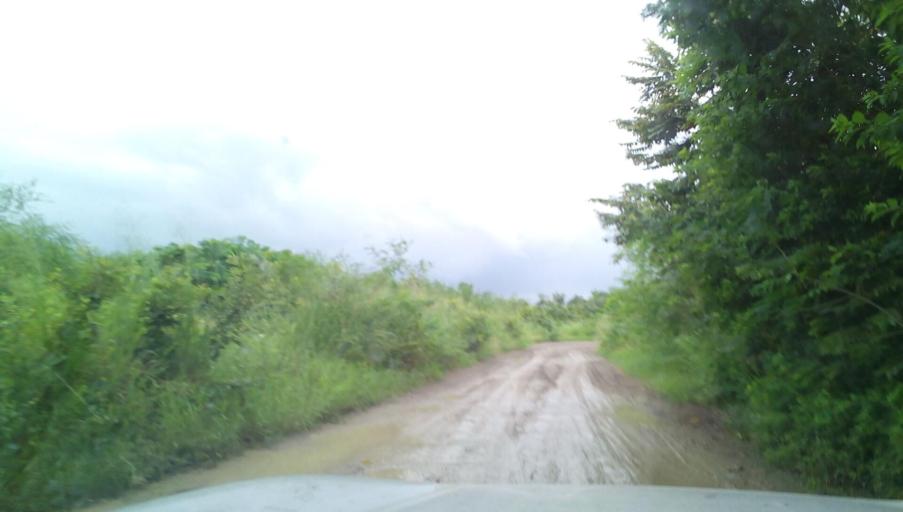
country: MX
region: Veracruz
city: Panuco
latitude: 21.8103
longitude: -98.1115
